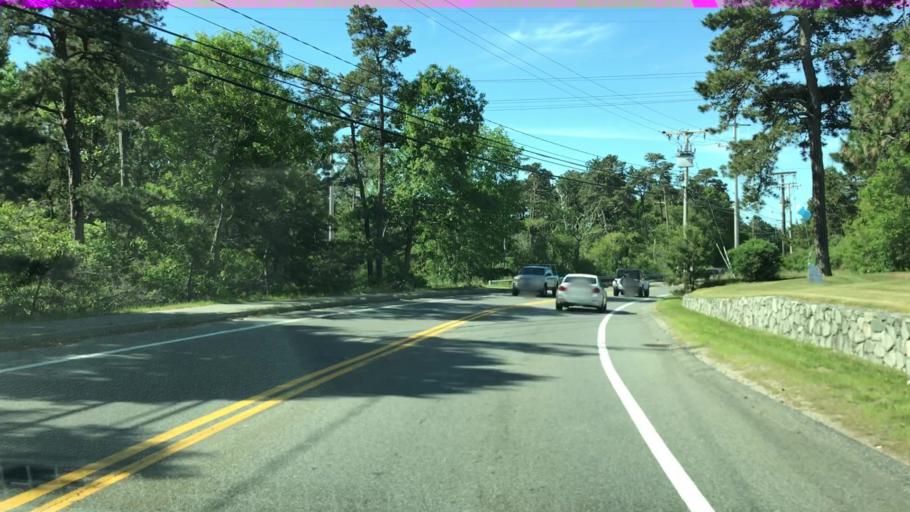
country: US
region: Massachusetts
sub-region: Barnstable County
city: Mashpee
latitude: 41.6099
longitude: -70.4908
